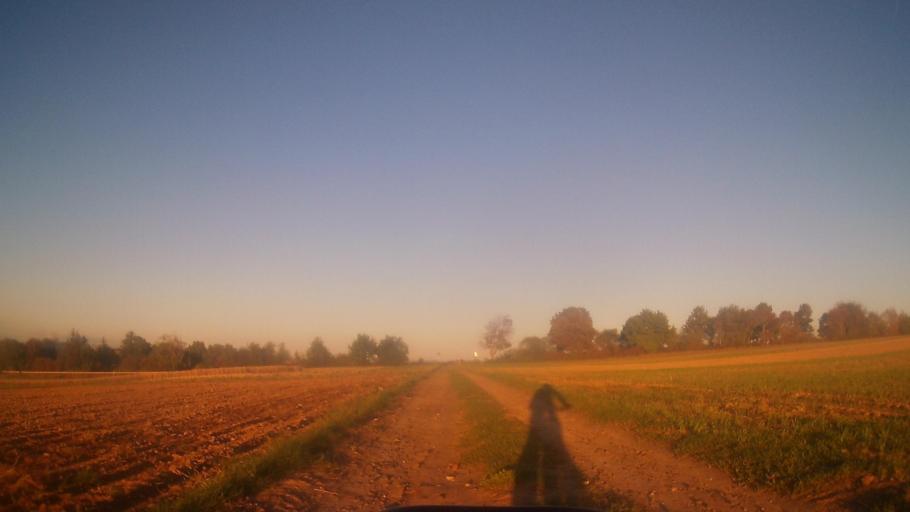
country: DE
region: Rheinland-Pfalz
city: Morstadt
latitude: 49.6279
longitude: 8.2790
